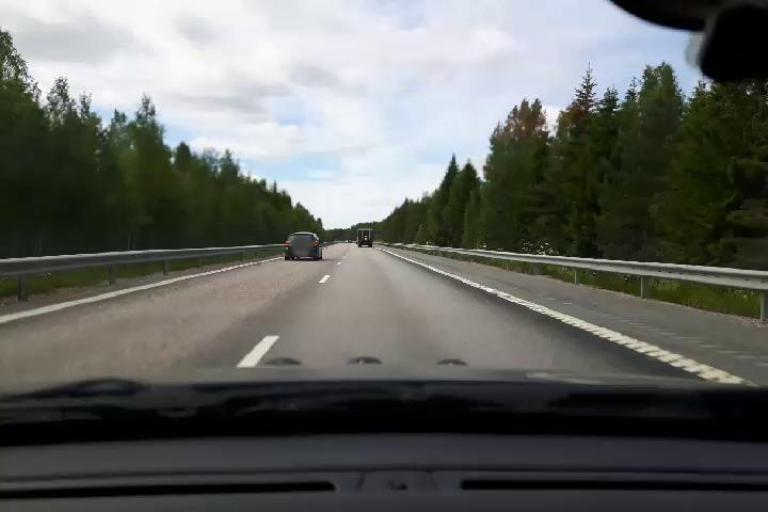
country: SE
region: Uppsala
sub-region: Alvkarleby Kommun
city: AElvkarleby
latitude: 60.4892
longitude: 17.3477
